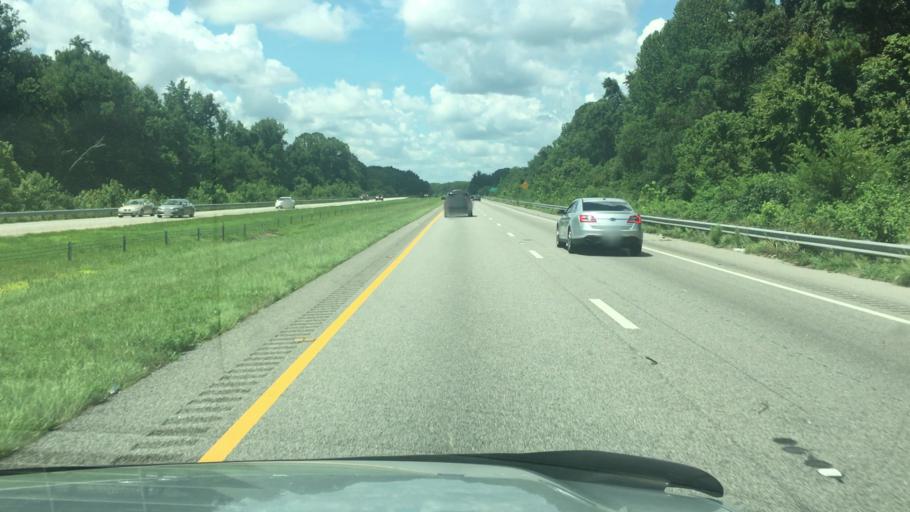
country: US
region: South Carolina
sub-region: Kershaw County
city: Camden
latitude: 34.2188
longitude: -80.6239
